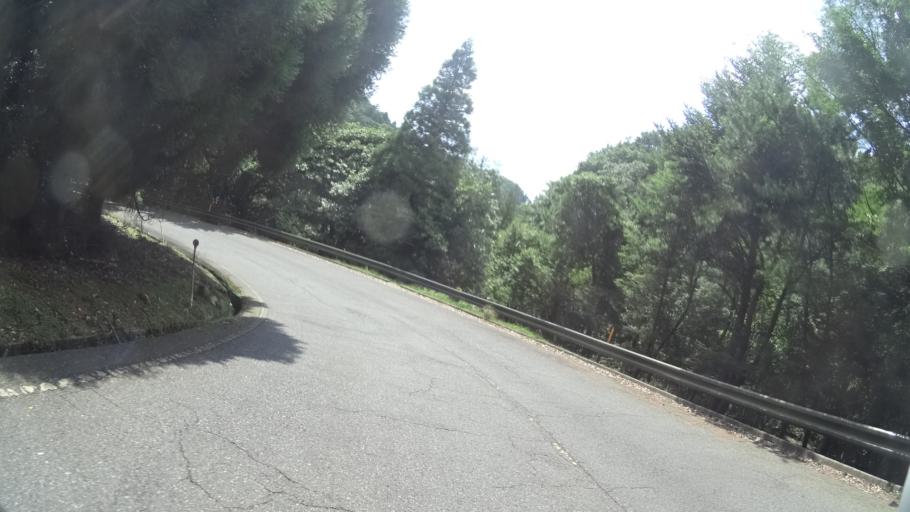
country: JP
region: Miyazaki
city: Kobayashi
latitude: 31.9029
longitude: 130.8450
